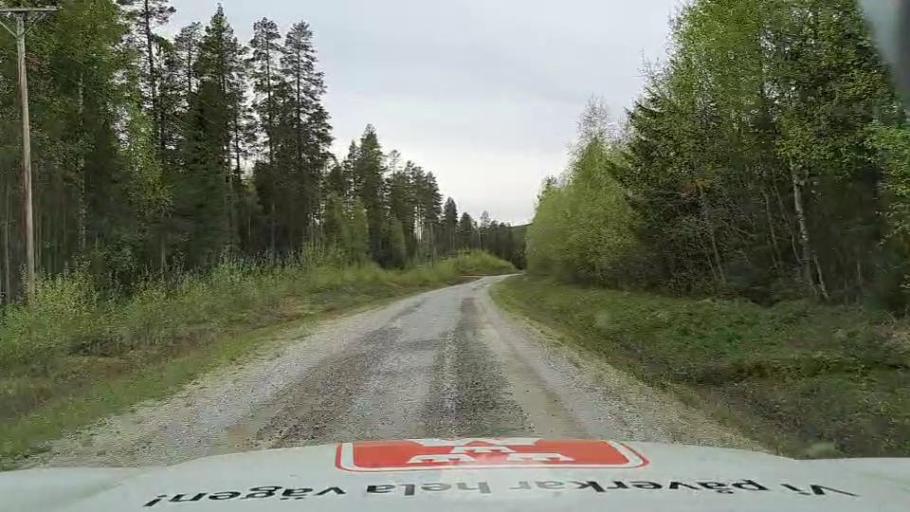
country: SE
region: Jaemtland
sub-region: Bergs Kommun
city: Hoverberg
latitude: 62.6752
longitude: 14.8012
